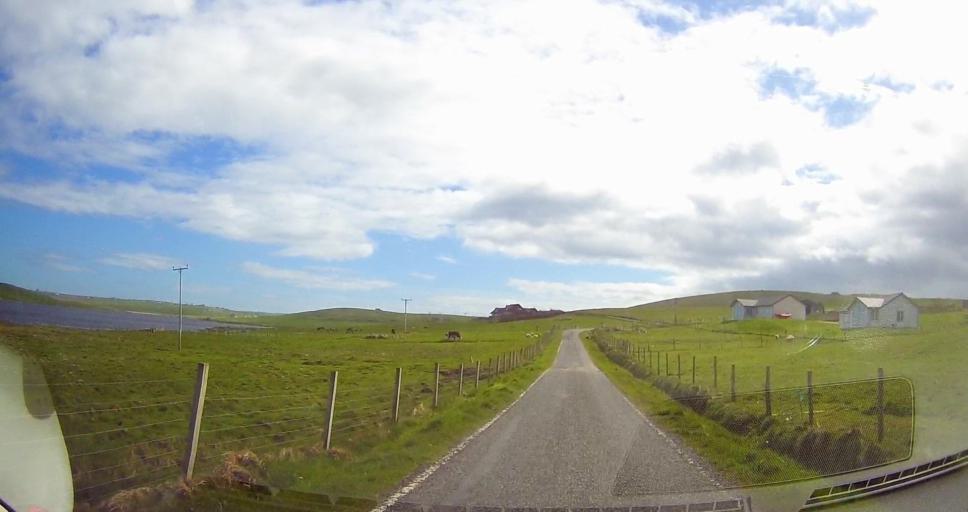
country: GB
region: Scotland
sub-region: Shetland Islands
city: Sandwick
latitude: 59.9348
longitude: -1.3458
